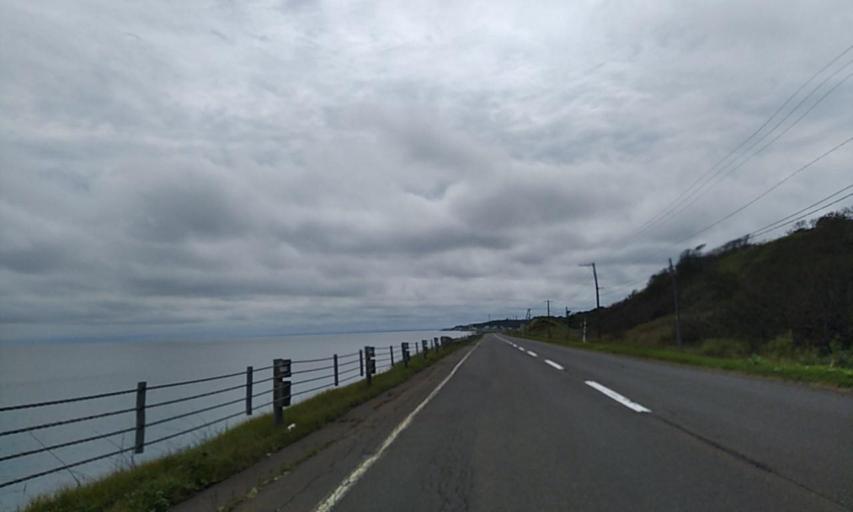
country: JP
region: Hokkaido
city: Shibetsu
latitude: 43.4989
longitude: 145.2471
